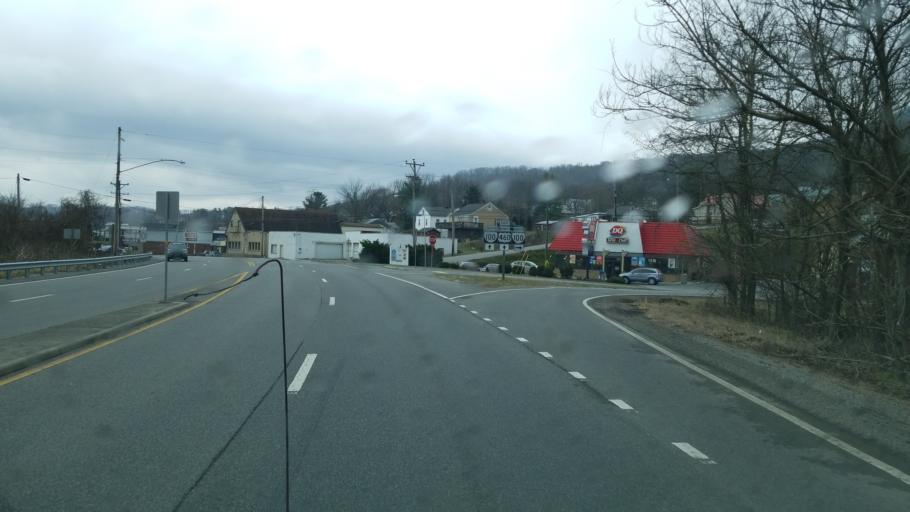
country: US
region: Virginia
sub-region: Giles County
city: Pearisburg
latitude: 37.3315
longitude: -80.7385
